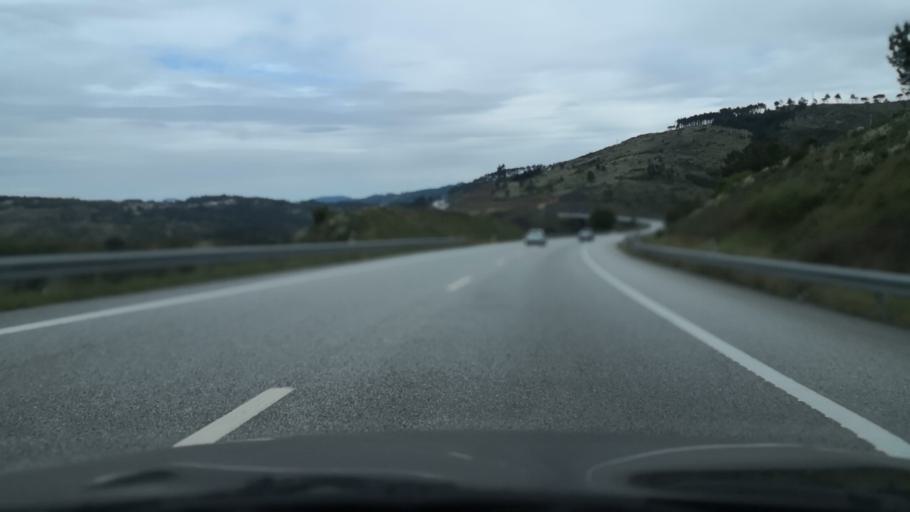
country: PT
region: Viseu
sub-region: Viseu
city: Rio de Loba
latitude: 40.6331
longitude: -7.8311
